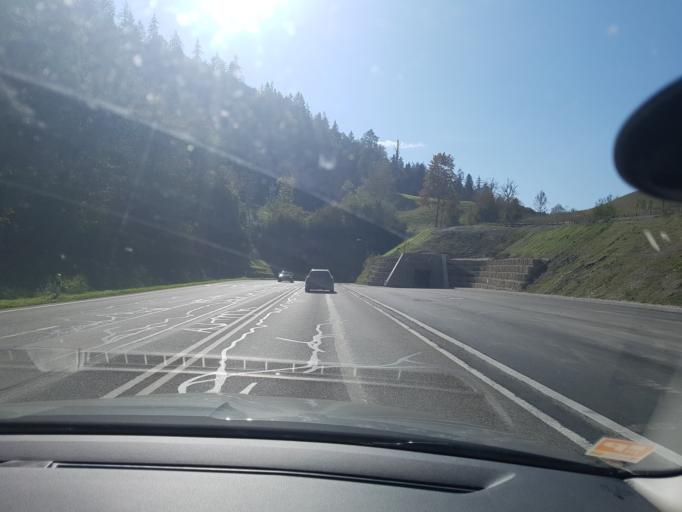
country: DE
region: Bavaria
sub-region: Upper Bavaria
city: Schneizlreuth
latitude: 47.6721
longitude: 12.7636
